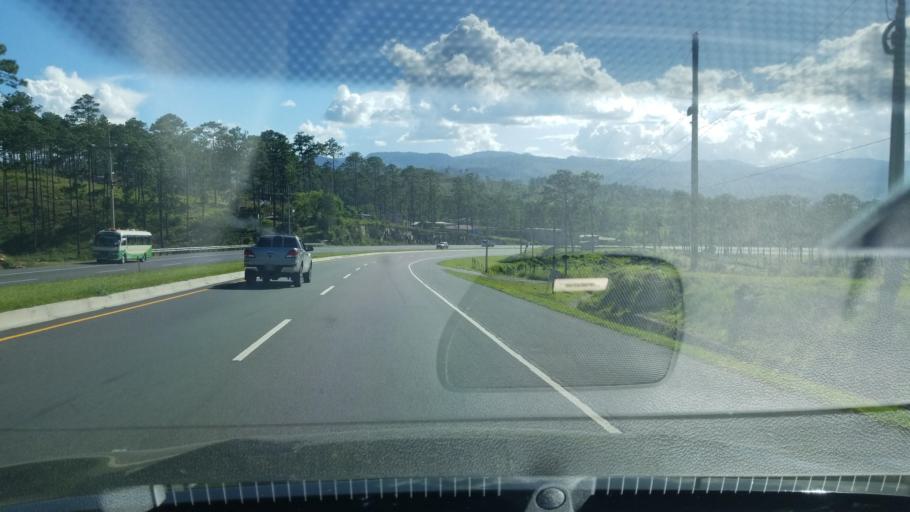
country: HN
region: Francisco Morazan
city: Tamara
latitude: 14.1677
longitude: -87.3094
